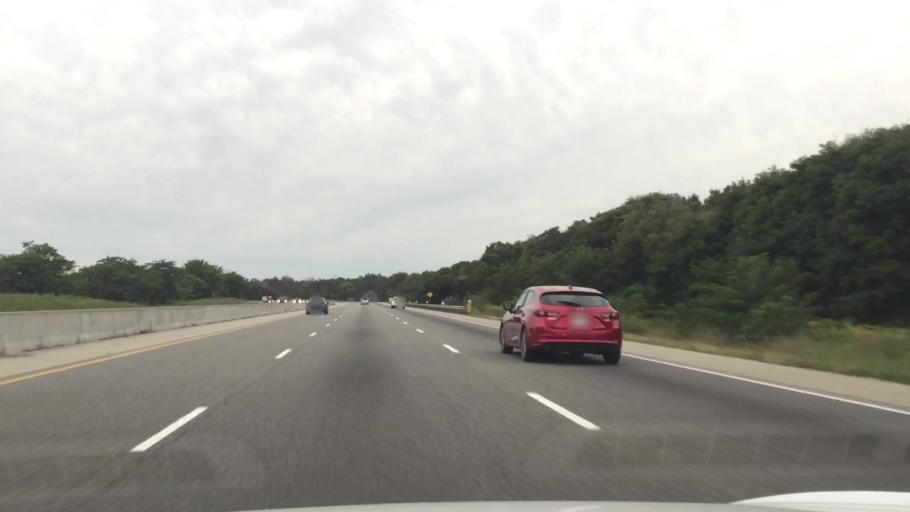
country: CA
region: Ontario
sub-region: Oxford County
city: Woodstock
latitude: 43.2361
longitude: -80.5906
